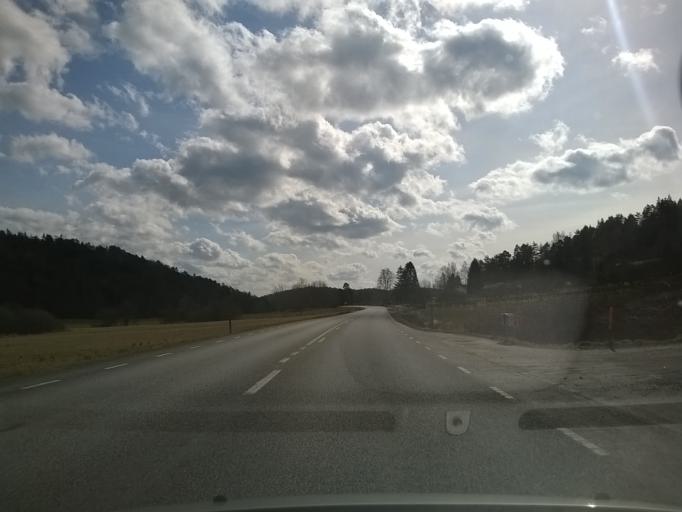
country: SE
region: Vaestra Goetaland
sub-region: Tjorns Kommun
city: Myggenas
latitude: 58.1398
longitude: 11.7123
